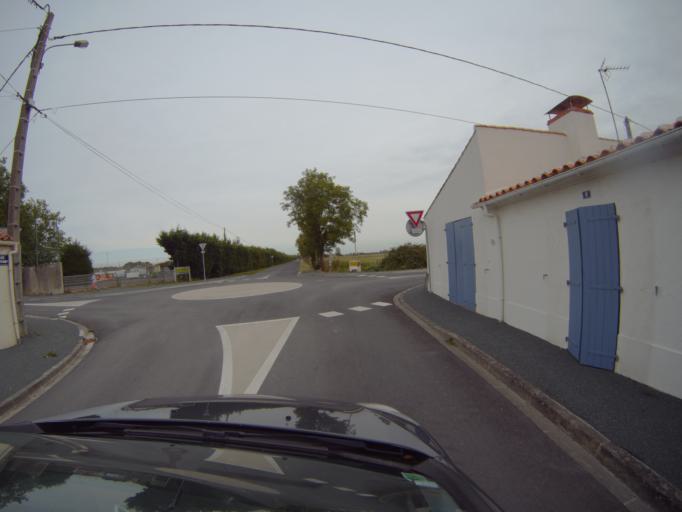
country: FR
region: Pays de la Loire
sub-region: Departement de la Vendee
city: Triaize
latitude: 46.3950
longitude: -1.1996
